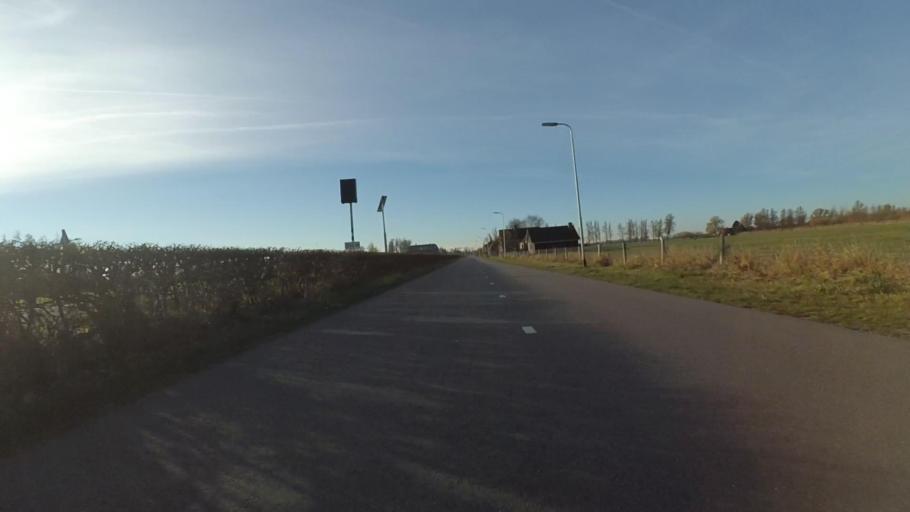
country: NL
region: Utrecht
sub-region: Gemeente Utrechtse Heuvelrug
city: Doorn
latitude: 52.0076
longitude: 5.3215
